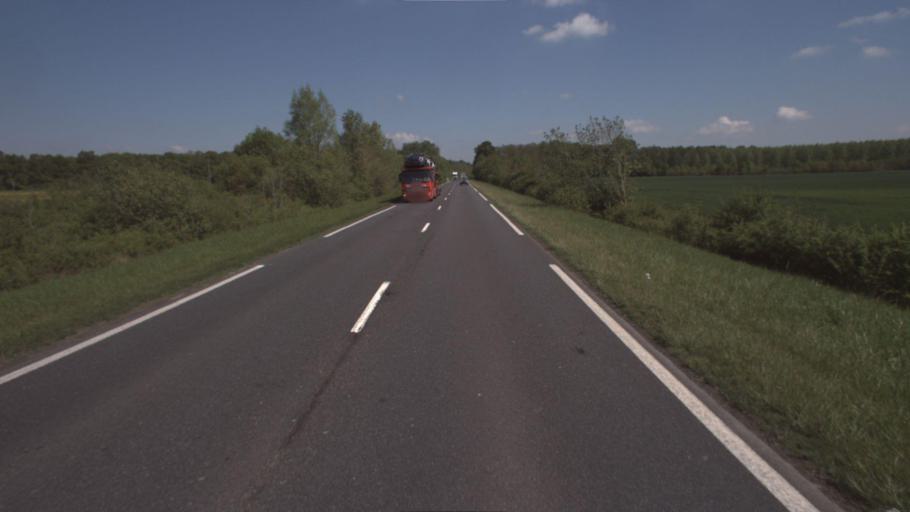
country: FR
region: Ile-de-France
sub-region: Departement de Seine-et-Marne
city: Chaumes-en-Brie
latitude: 48.6792
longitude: 2.8142
